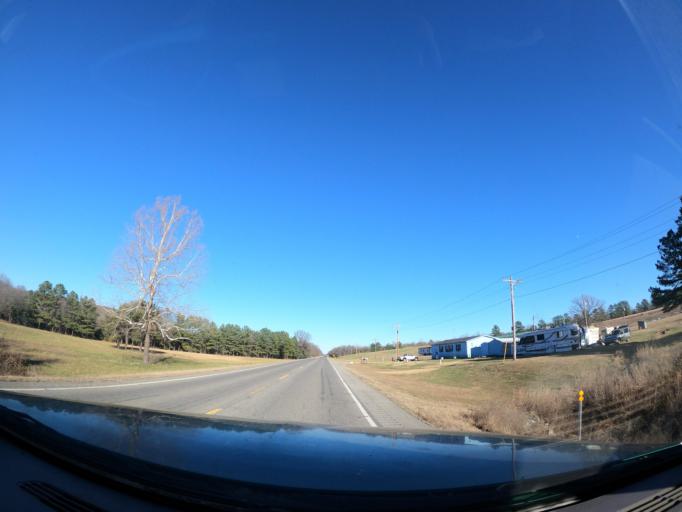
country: US
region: Oklahoma
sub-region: Pittsburg County
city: Quinton
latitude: 35.2161
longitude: -95.4102
